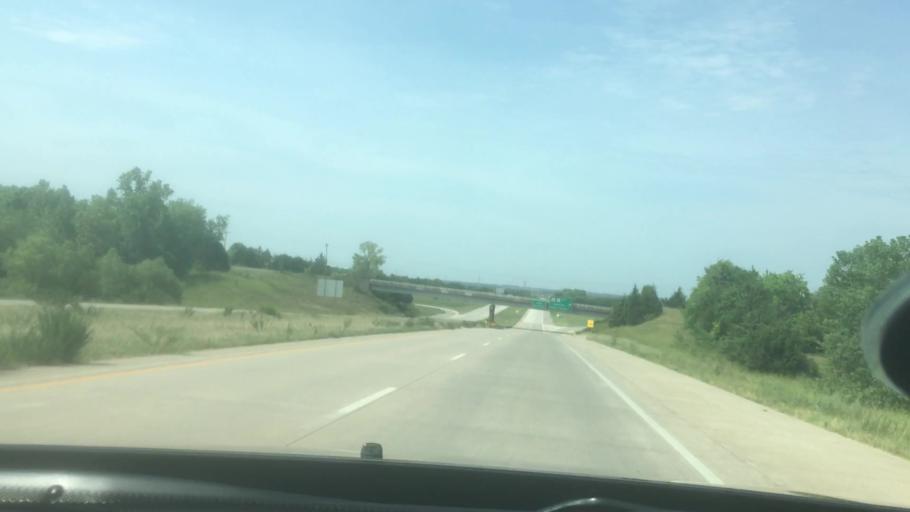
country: US
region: Oklahoma
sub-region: Pontotoc County
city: Ada
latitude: 34.7816
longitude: -96.6988
